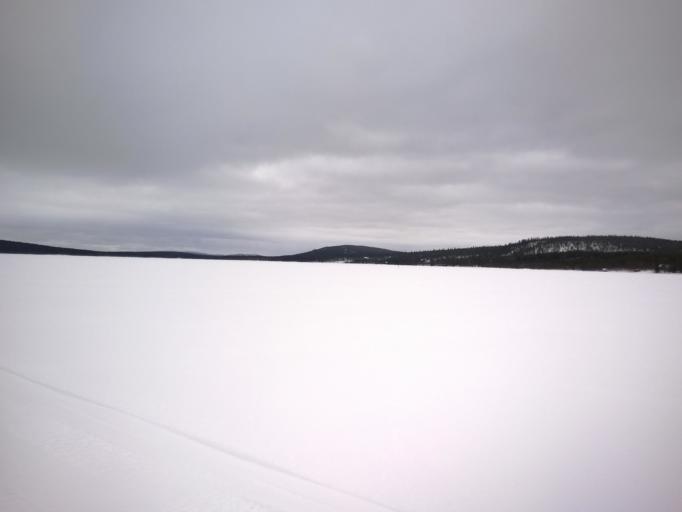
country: FI
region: Lapland
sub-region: Tunturi-Lappi
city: Muonio
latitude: 67.9091
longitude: 23.9441
